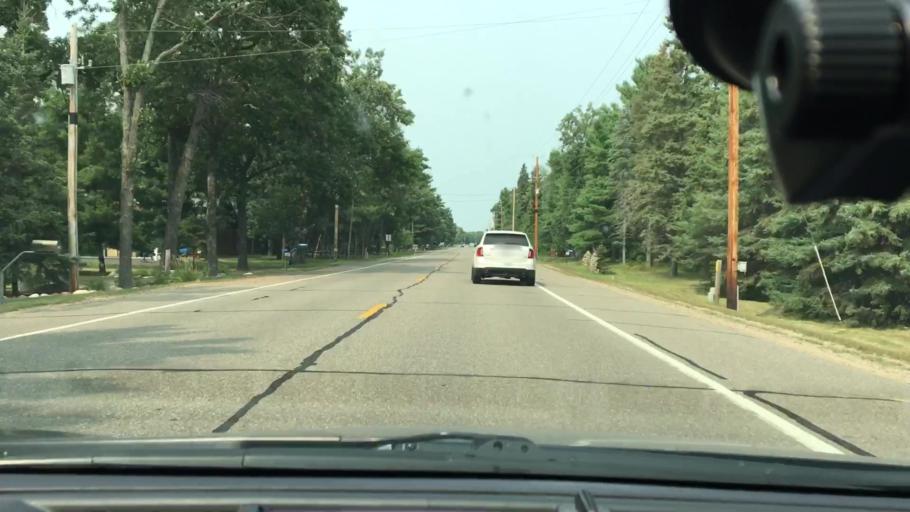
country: US
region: Minnesota
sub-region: Crow Wing County
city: Cross Lake
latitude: 46.5867
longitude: -94.1315
